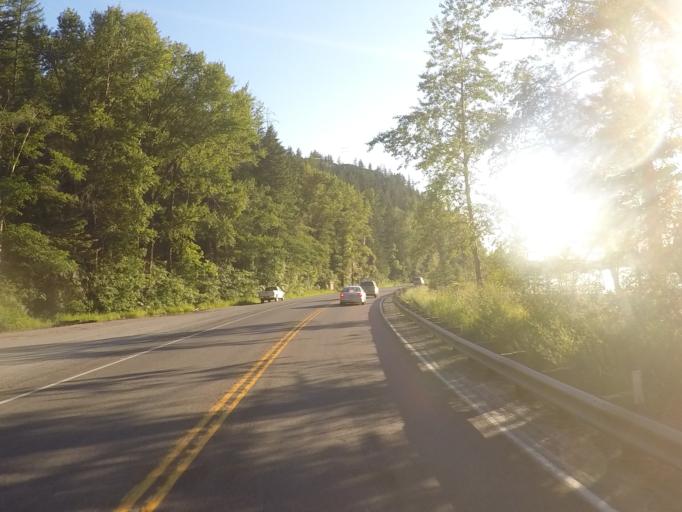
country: US
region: Montana
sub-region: Flathead County
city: Columbia Falls
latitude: 48.3859
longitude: -114.1023
